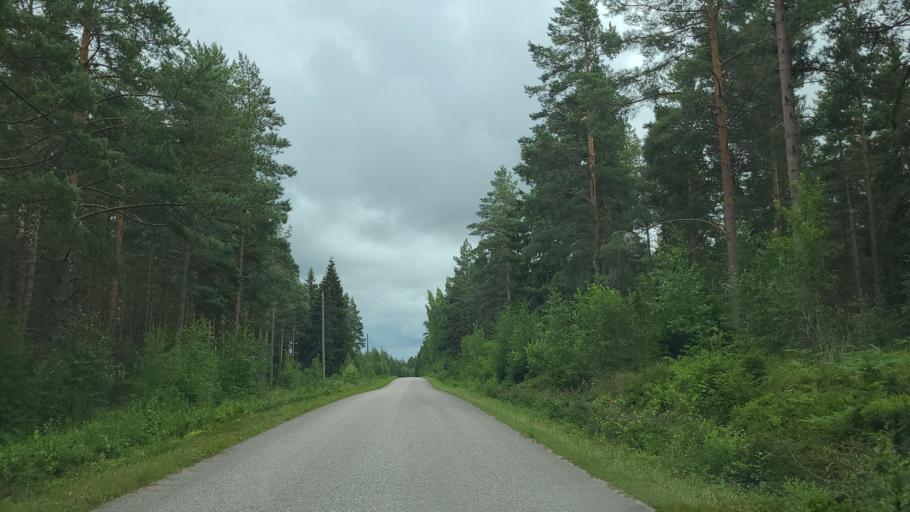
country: FI
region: Varsinais-Suomi
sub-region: Aboland-Turunmaa
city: Dragsfjaerd
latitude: 60.0786
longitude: 22.4251
